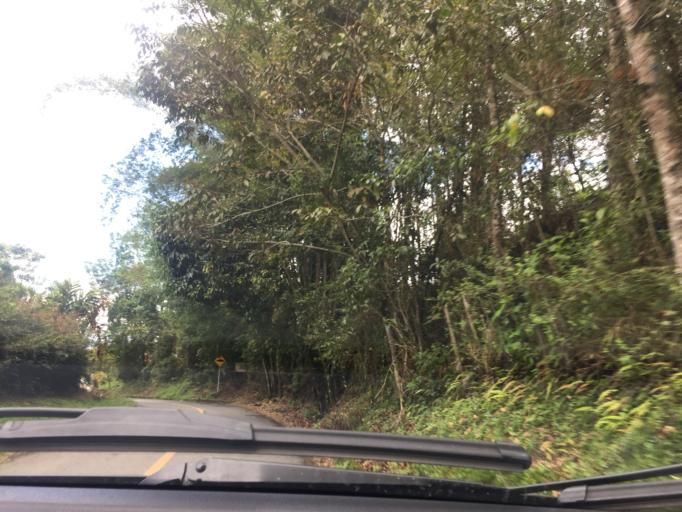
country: CO
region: Cundinamarca
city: Supata
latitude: 5.0581
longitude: -74.2349
